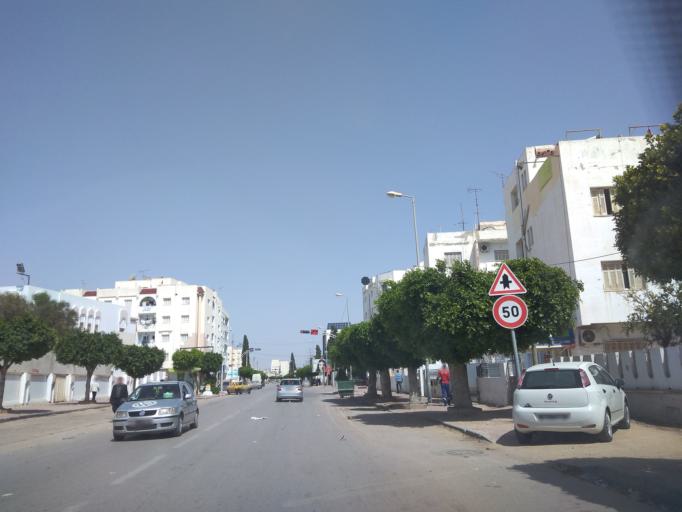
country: TN
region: Safaqis
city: Sfax
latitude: 34.7423
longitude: 10.7503
